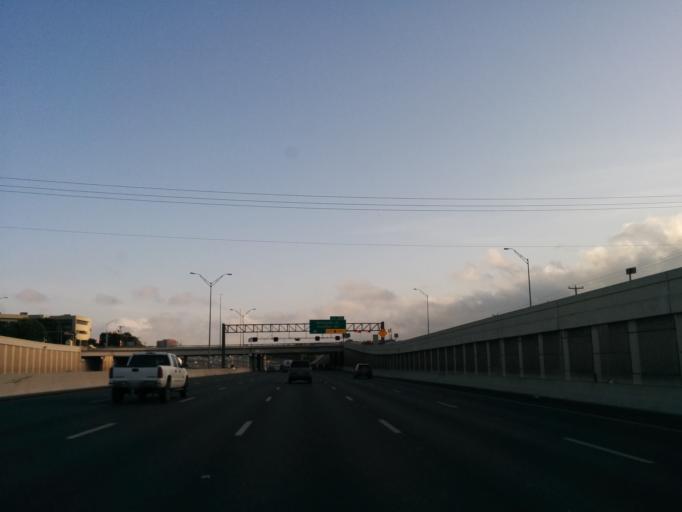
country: US
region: Texas
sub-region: Bexar County
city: Balcones Heights
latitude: 29.5212
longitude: -98.5551
